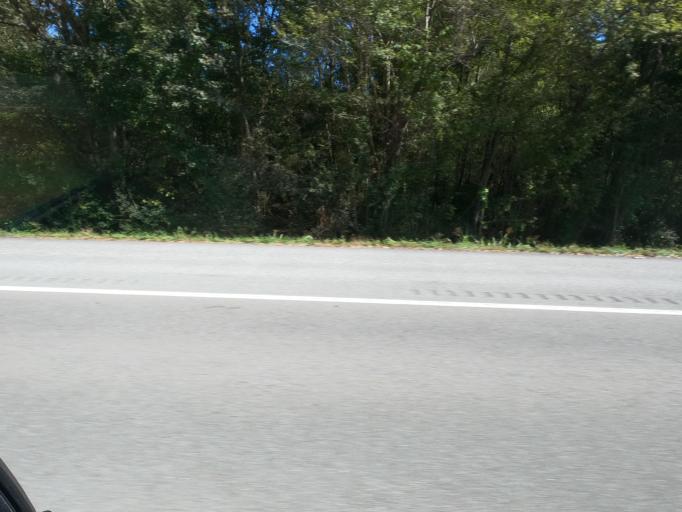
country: US
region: Tennessee
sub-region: Maury County
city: Mount Pleasant
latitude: 35.4166
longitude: -87.2819
